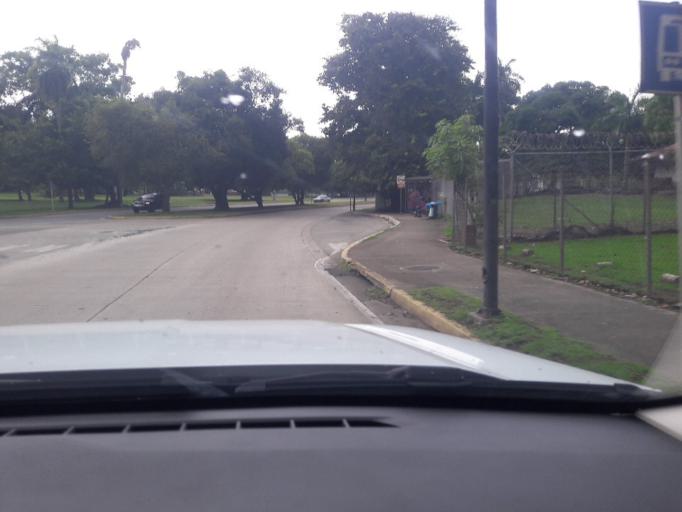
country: PA
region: Panama
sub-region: Distrito de Panama
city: Ancon
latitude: 8.9406
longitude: -79.5515
